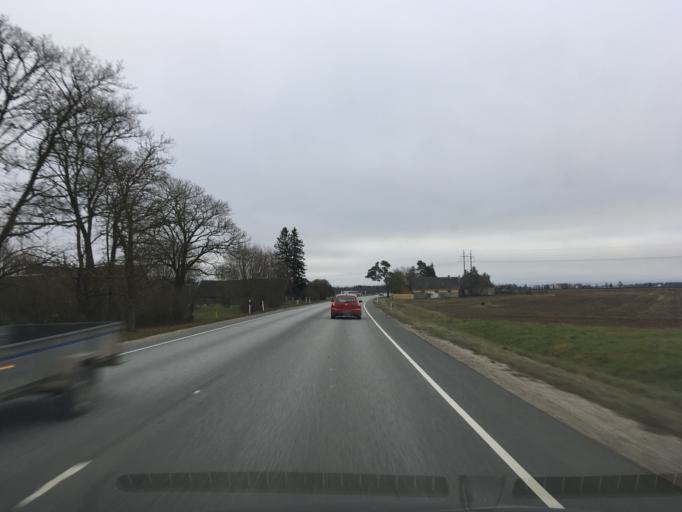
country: EE
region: Laeaene-Virumaa
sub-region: Someru vald
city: Someru
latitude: 59.3772
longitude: 26.4194
